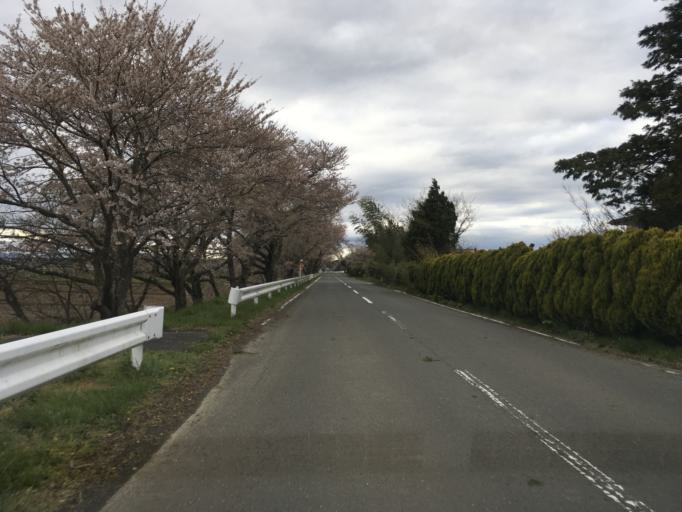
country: JP
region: Miyagi
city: Wakuya
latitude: 38.6477
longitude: 141.1453
